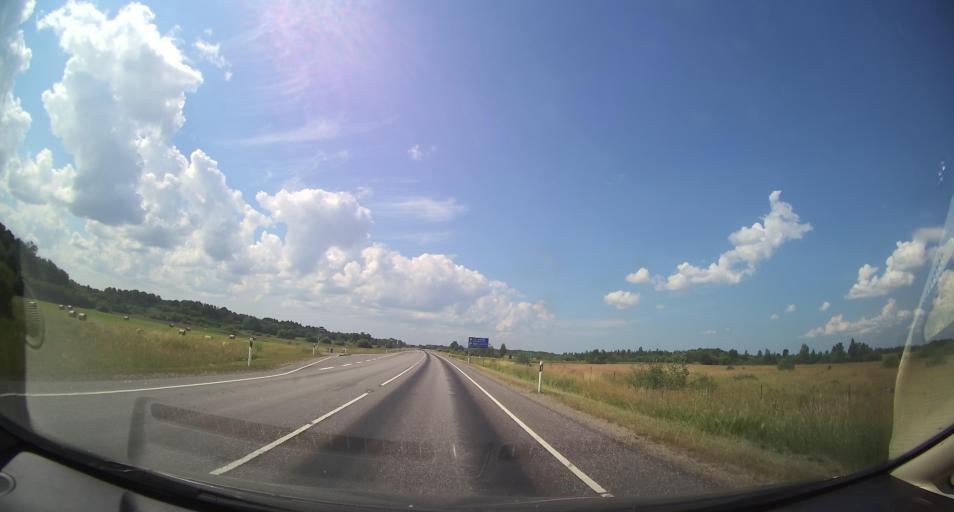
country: EE
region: Laeaene
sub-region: Lihula vald
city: Lihula
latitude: 58.7241
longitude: 23.9199
